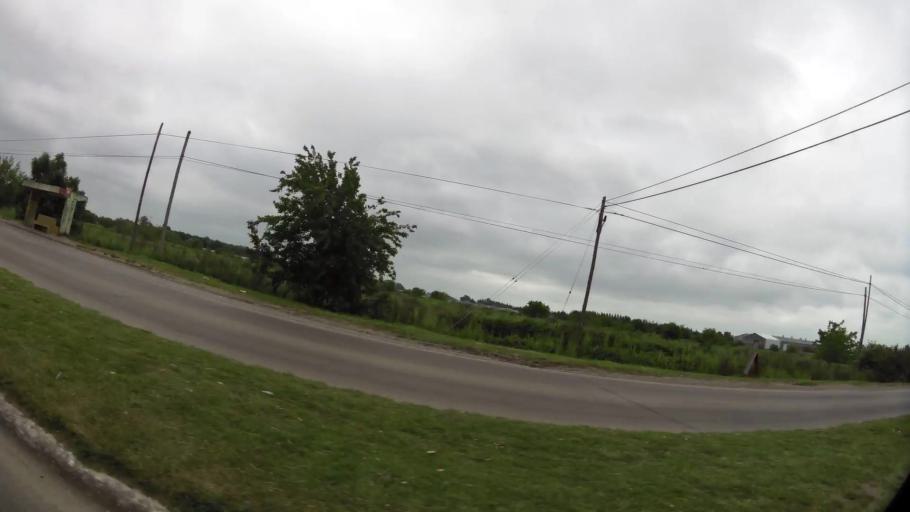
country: AR
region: Buenos Aires
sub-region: Partido de La Plata
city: La Plata
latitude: -35.0029
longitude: -58.0565
